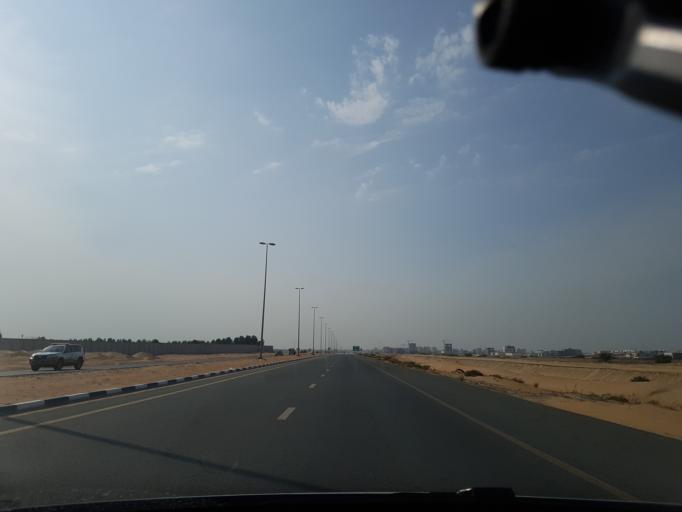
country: AE
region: Ajman
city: Ajman
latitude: 25.4123
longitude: 55.5621
